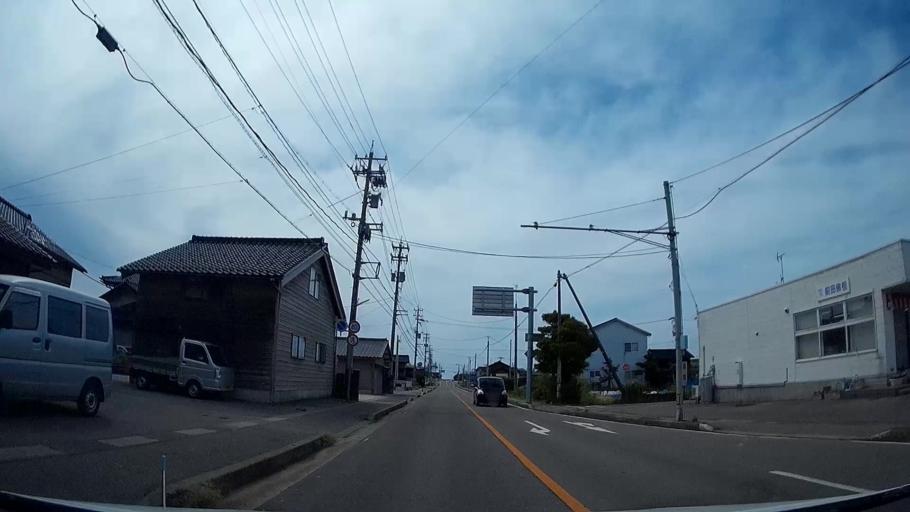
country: JP
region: Ishikawa
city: Hakui
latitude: 36.9966
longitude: 136.7766
